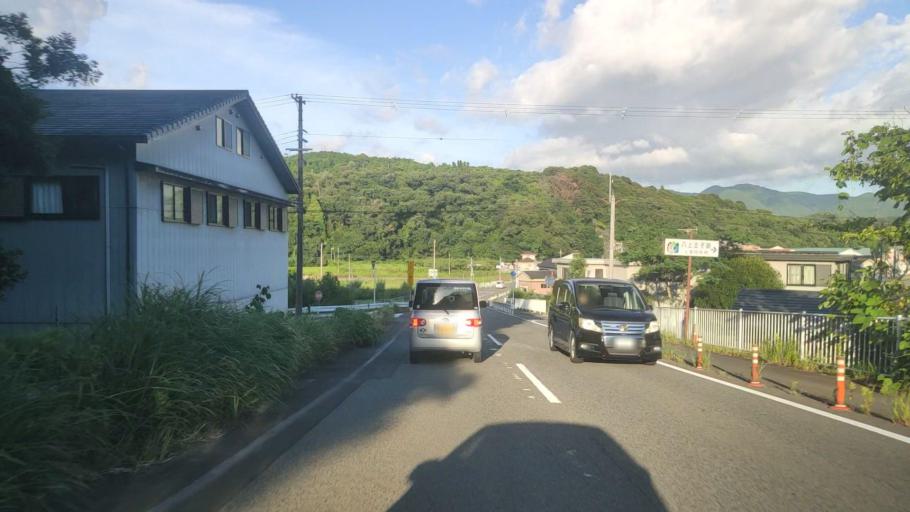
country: JP
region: Wakayama
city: Tanabe
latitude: 33.7267
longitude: 135.4405
